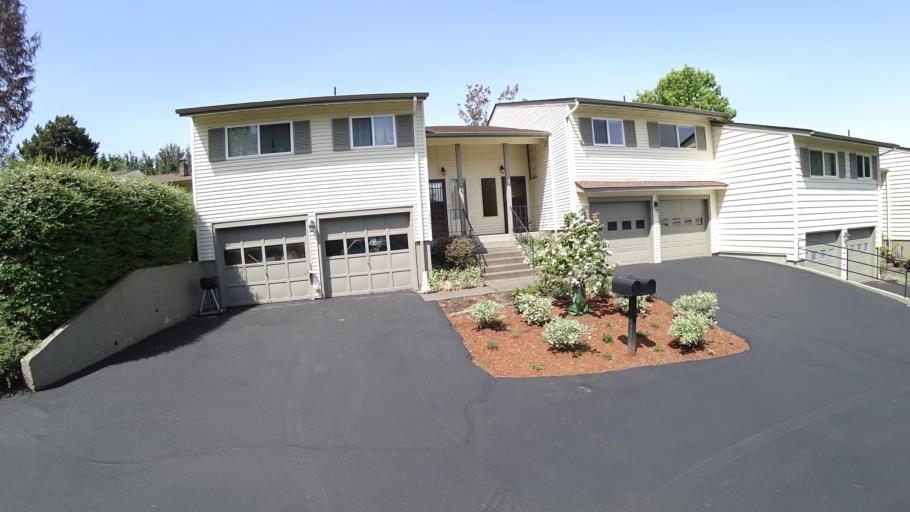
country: US
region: Oregon
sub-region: Multnomah County
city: Fairview
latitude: 45.5464
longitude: -122.5083
